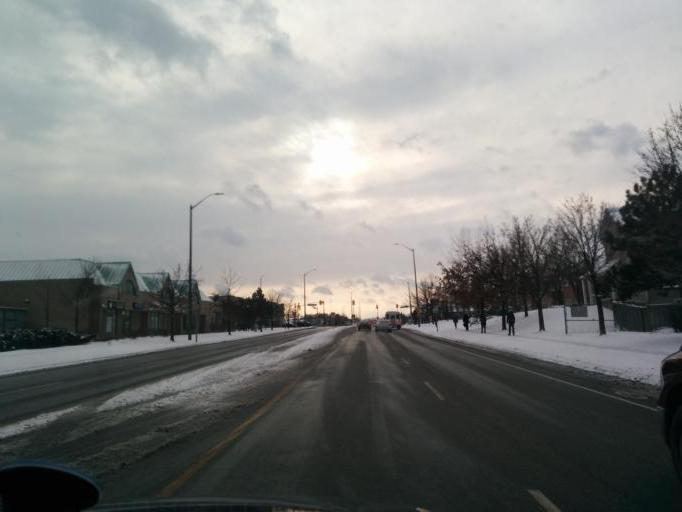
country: CA
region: Ontario
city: Mississauga
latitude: 43.5589
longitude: -79.7163
